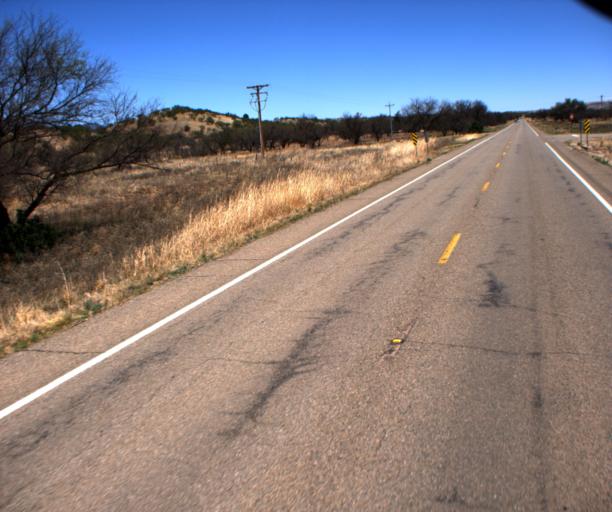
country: US
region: Arizona
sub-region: Santa Cruz County
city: Rio Rico
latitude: 31.5728
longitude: -110.7299
